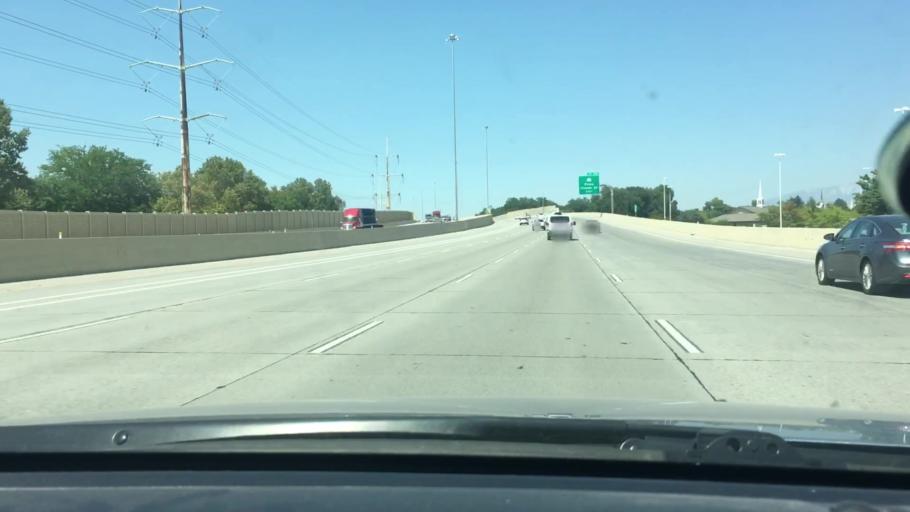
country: US
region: Utah
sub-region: Utah County
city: Provo
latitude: 40.2149
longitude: -111.6644
